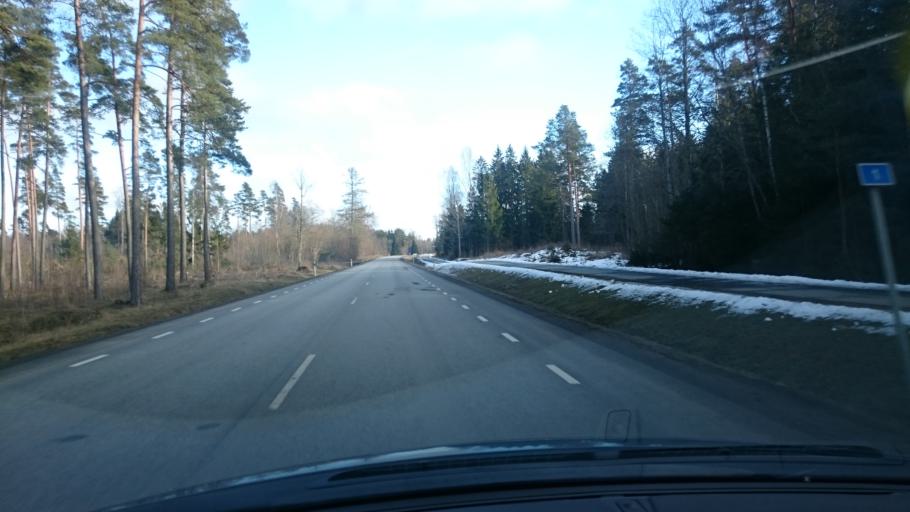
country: EE
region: Harju
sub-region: Kiili vald
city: Kiili
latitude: 59.3520
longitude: 24.7888
